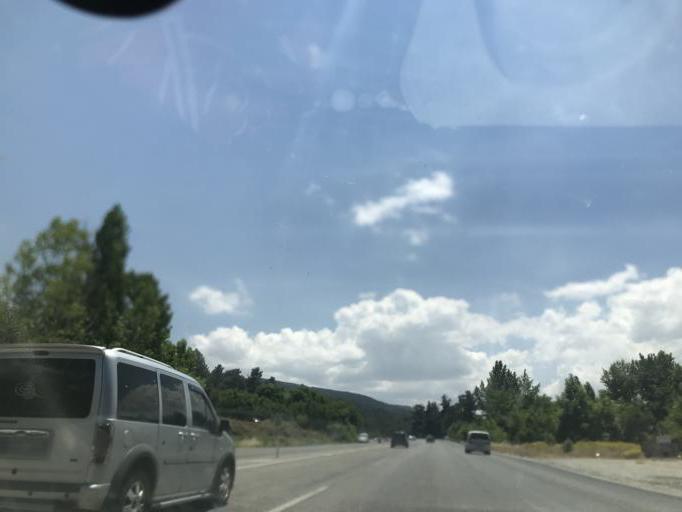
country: TR
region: Denizli
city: Serinhisar
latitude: 37.6691
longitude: 29.2282
